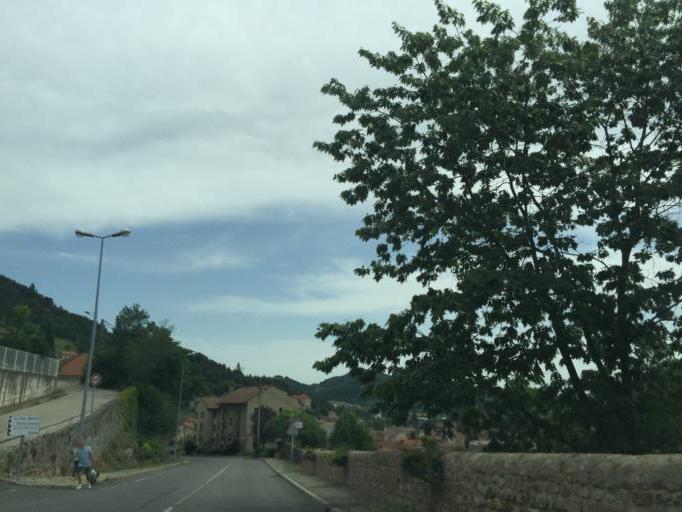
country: FR
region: Rhone-Alpes
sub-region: Departement de la Loire
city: Bourg-Argental
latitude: 45.2946
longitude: 4.5552
